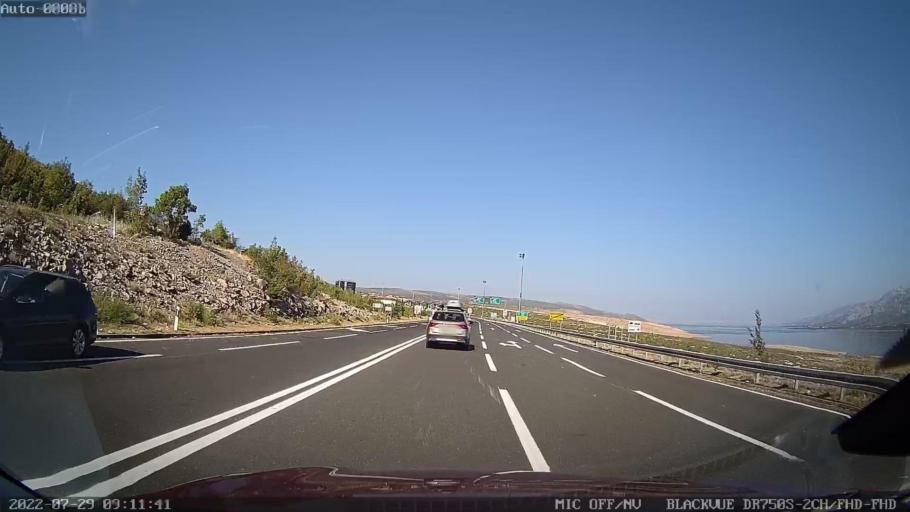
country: HR
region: Zadarska
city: Posedarje
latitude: 44.2431
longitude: 15.5378
